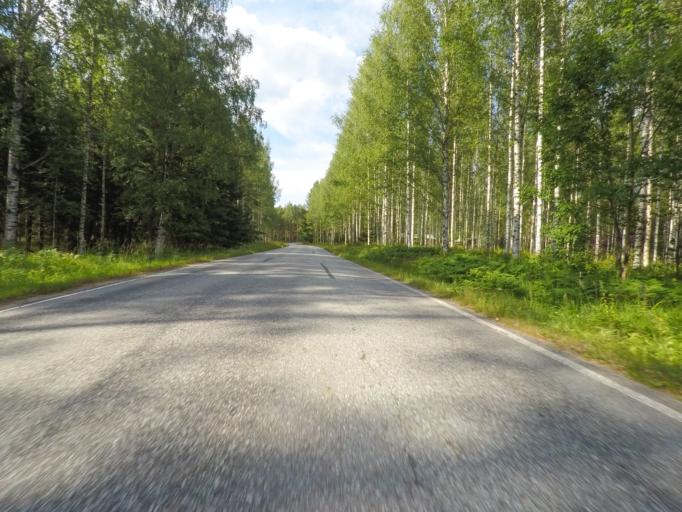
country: FI
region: Southern Savonia
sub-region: Mikkeli
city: Puumala
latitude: 61.6990
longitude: 28.2122
